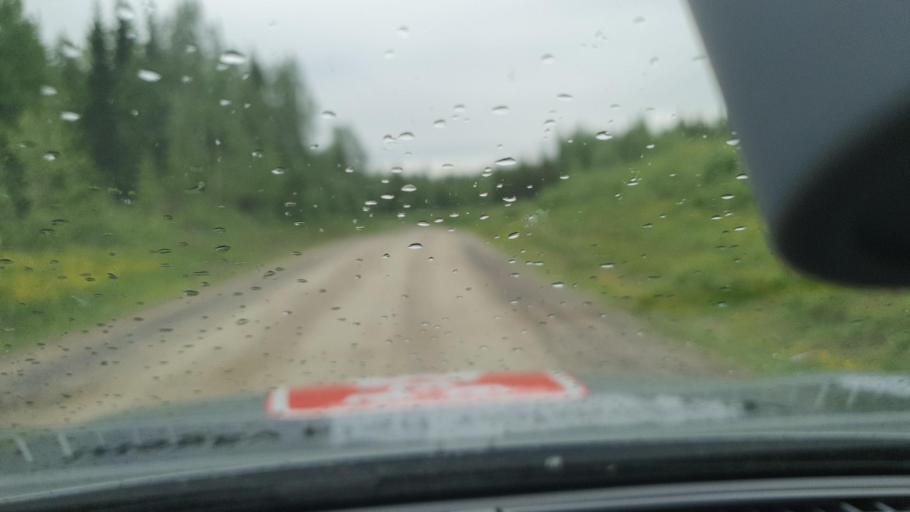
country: SE
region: Norrbotten
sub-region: Kalix Kommun
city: Rolfs
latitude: 66.0713
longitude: 22.9806
